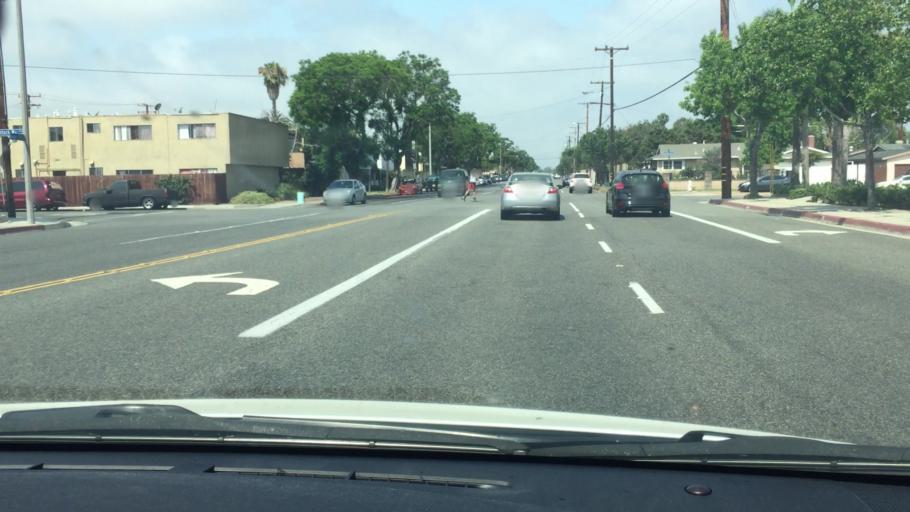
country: US
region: California
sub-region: Orange County
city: Costa Mesa
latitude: 33.6802
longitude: -117.9092
